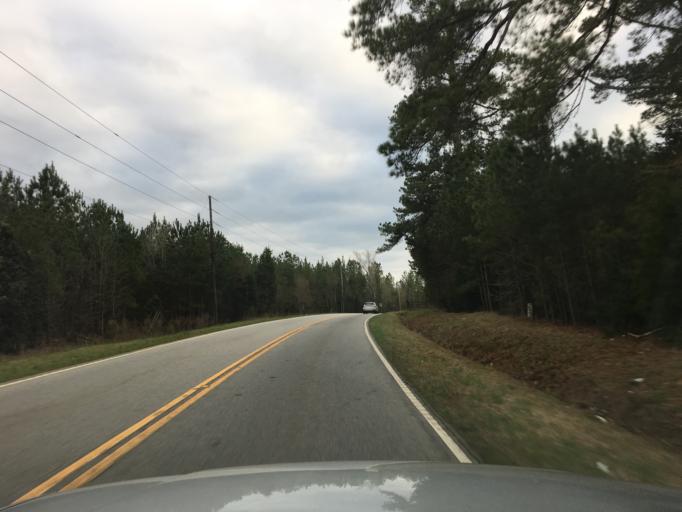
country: US
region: South Carolina
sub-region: Saluda County
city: Saluda
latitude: 33.9839
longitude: -81.7693
